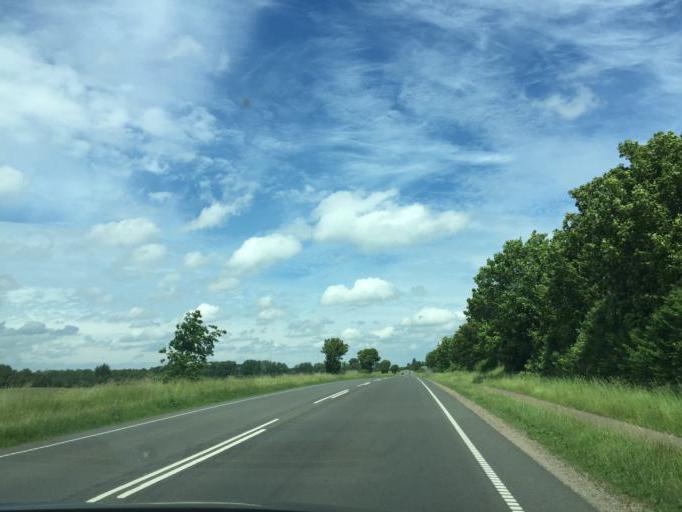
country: DK
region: South Denmark
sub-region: Odense Kommune
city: Hojby
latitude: 55.3086
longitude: 10.3980
